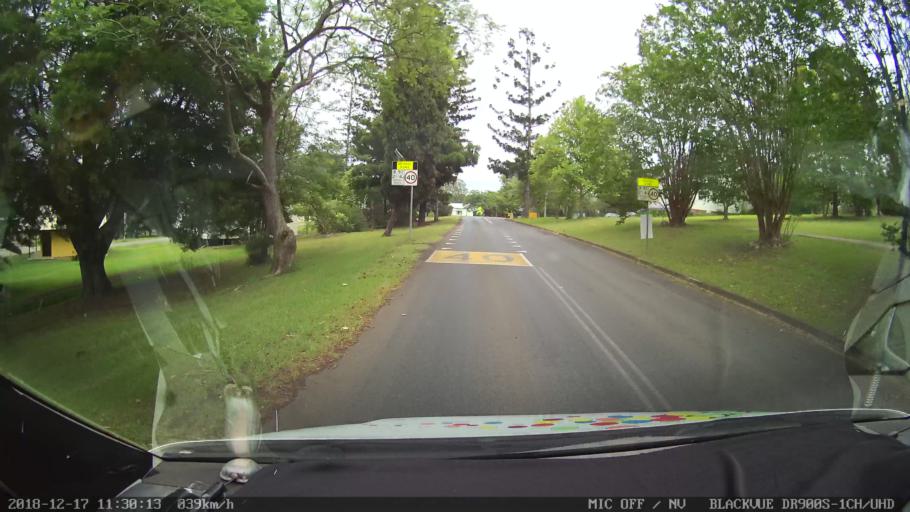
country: AU
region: New South Wales
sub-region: Kyogle
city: Kyogle
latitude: -28.7372
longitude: 152.6245
